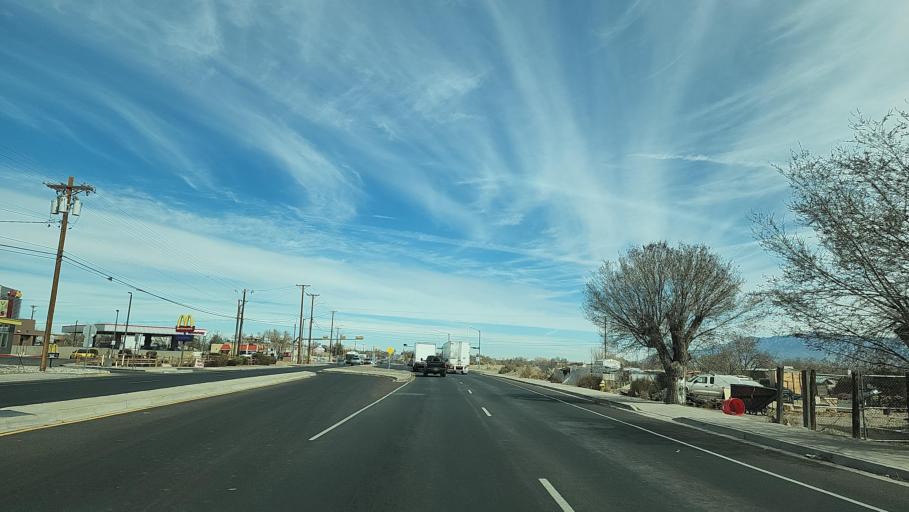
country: US
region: New Mexico
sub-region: Bernalillo County
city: South Valley
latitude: 35.0498
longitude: -106.7078
